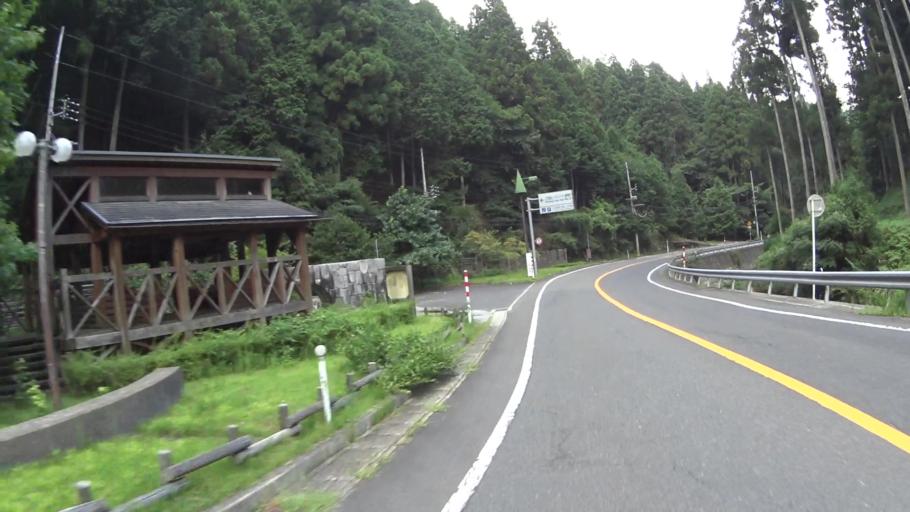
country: JP
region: Kyoto
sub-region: Kyoto-shi
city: Kamigyo-ku
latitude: 35.2324
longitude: 135.6624
